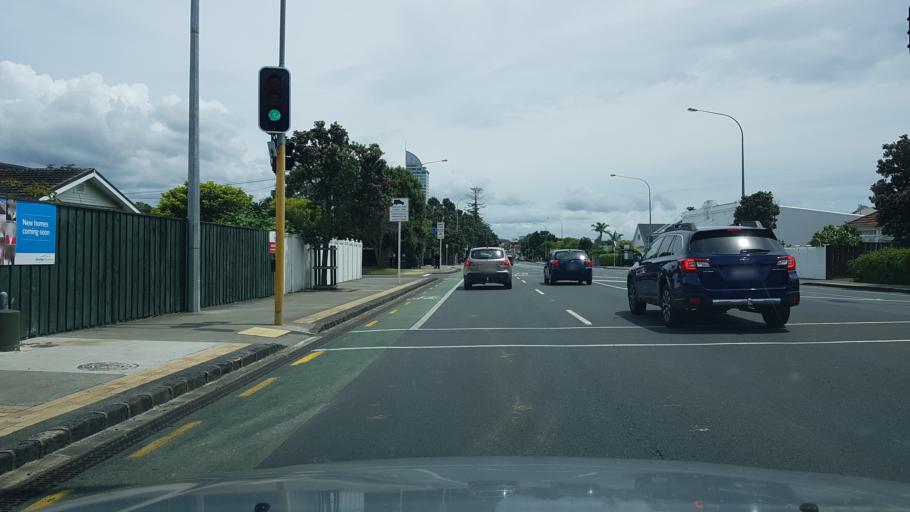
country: NZ
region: Auckland
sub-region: Auckland
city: North Shore
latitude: -36.7954
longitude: 174.7772
